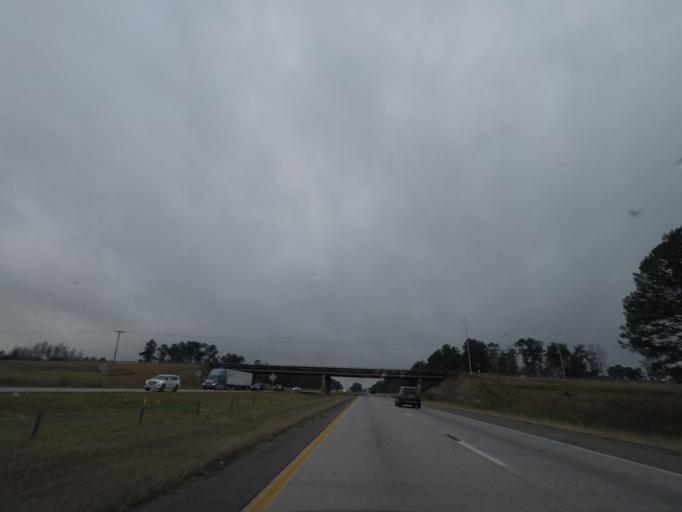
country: US
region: South Carolina
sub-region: Dorchester County
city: Saint George
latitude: 33.0856
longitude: -80.6523
